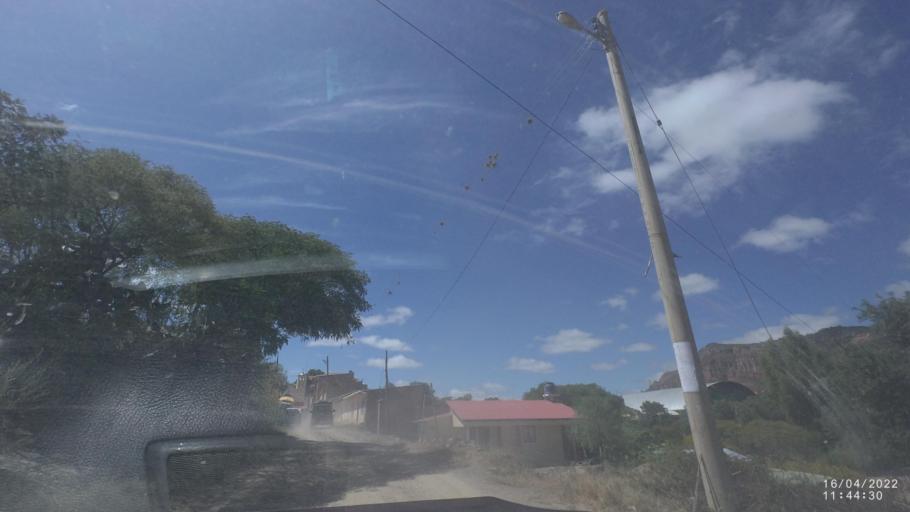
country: BO
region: Cochabamba
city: Mizque
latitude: -17.9850
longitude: -65.6308
